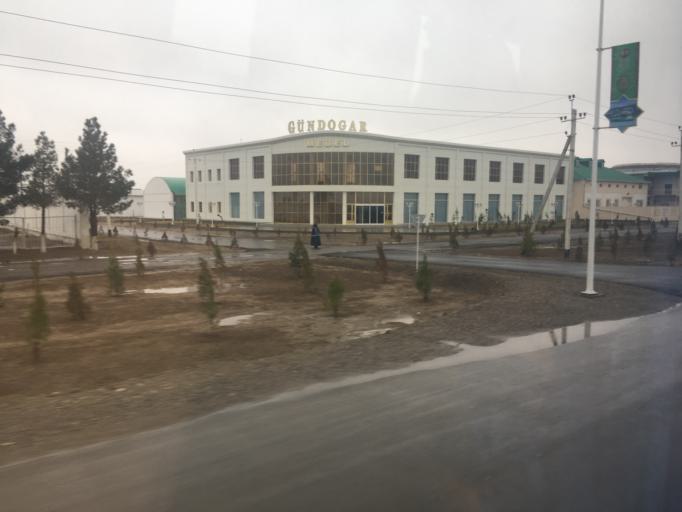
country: TM
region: Lebap
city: Turkmenabat
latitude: 38.9884
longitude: 63.5747
